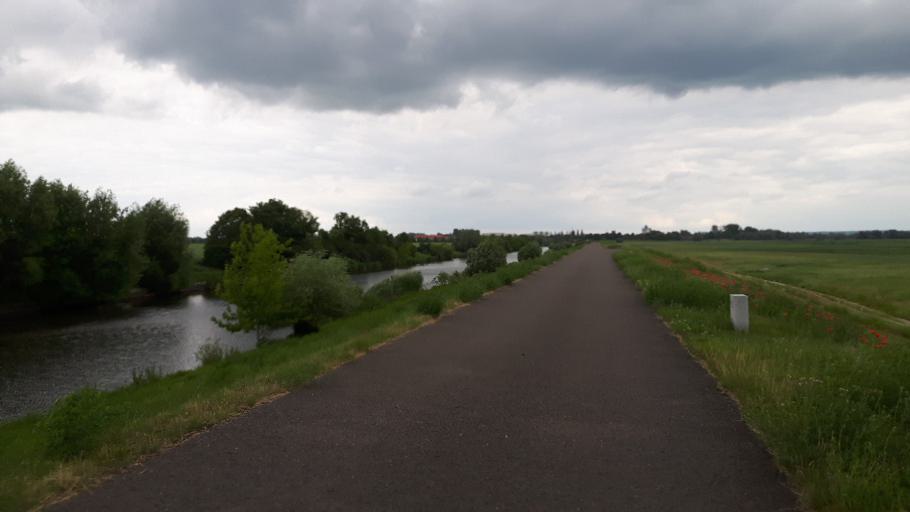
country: DE
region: Brandenburg
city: Meyenburg
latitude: 53.0372
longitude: 14.2604
